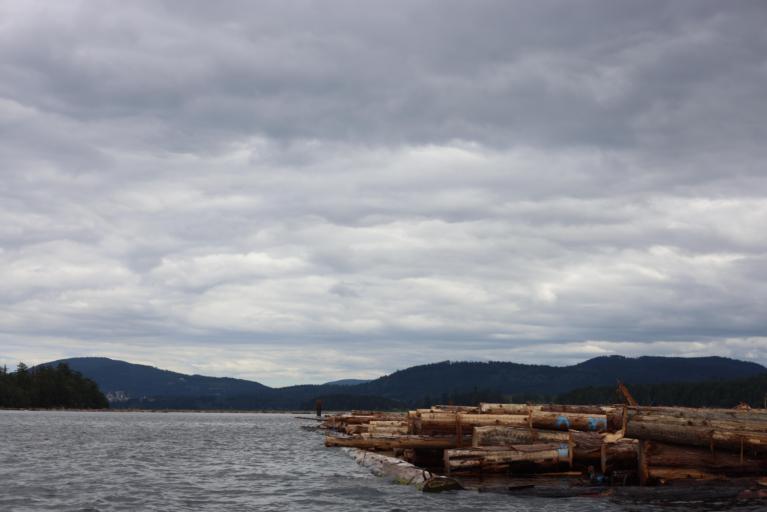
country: CA
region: British Columbia
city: North Cowichan
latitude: 48.9175
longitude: -123.6891
